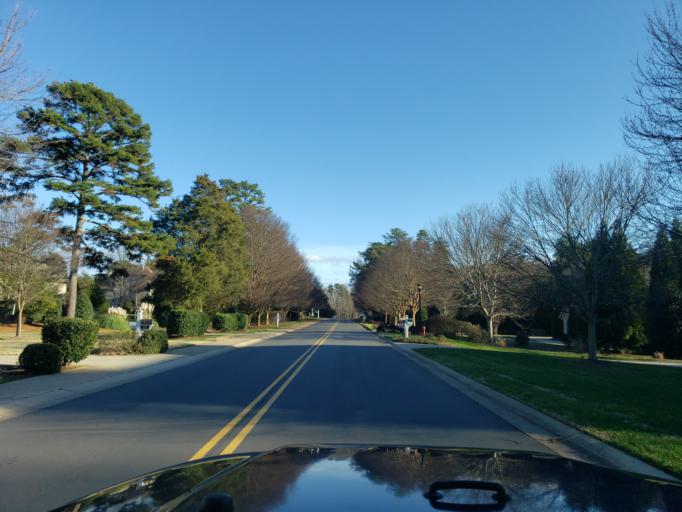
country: US
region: North Carolina
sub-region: Lincoln County
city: Westport
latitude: 35.5261
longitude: -80.9235
